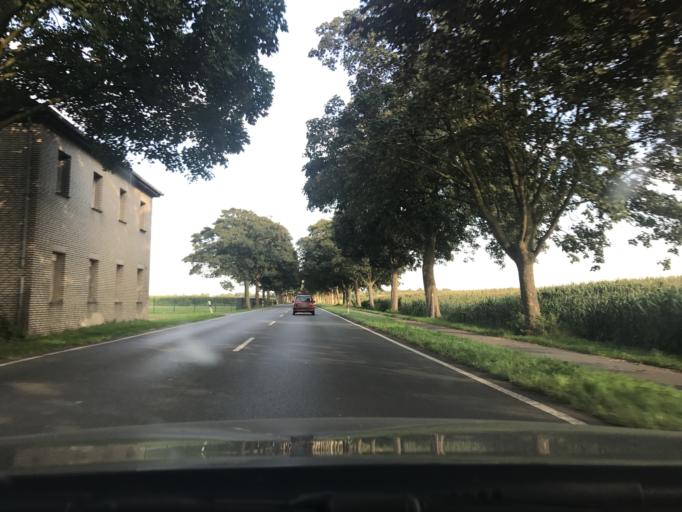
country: DE
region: North Rhine-Westphalia
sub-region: Regierungsbezirk Dusseldorf
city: Wachtendonk
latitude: 51.4468
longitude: 6.3973
